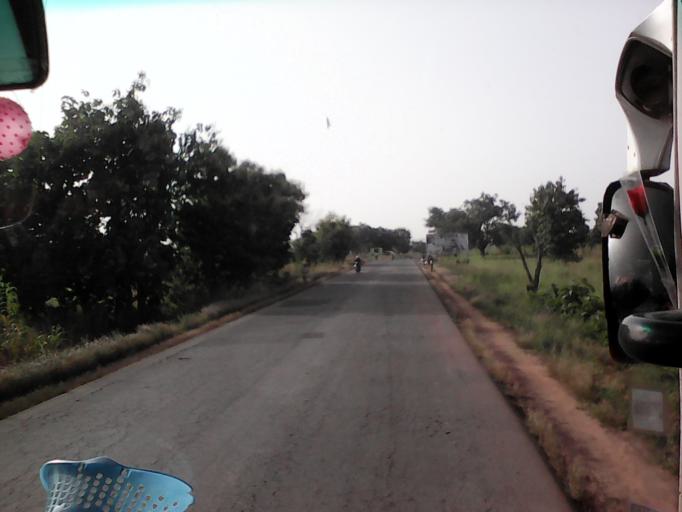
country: TG
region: Kara
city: Kara
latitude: 9.5180
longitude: 1.2089
